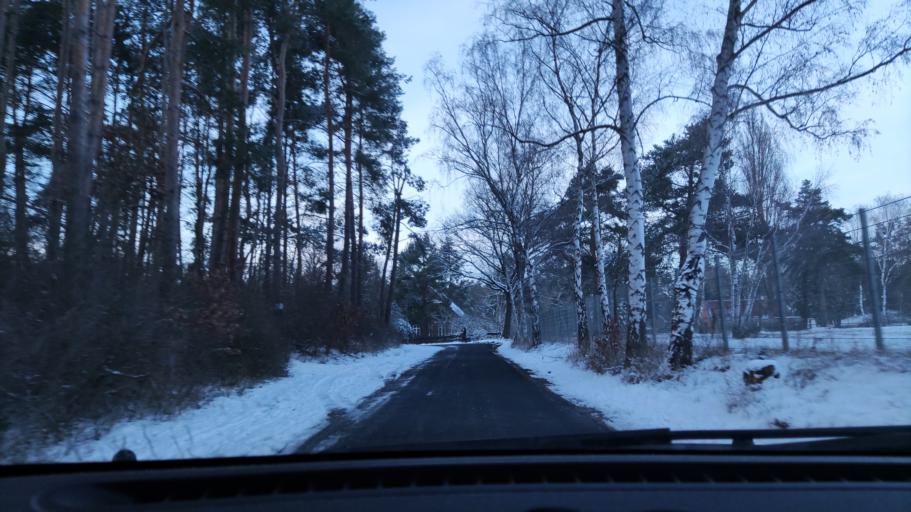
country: DE
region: Lower Saxony
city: Tosterglope
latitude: 53.2695
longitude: 10.8007
